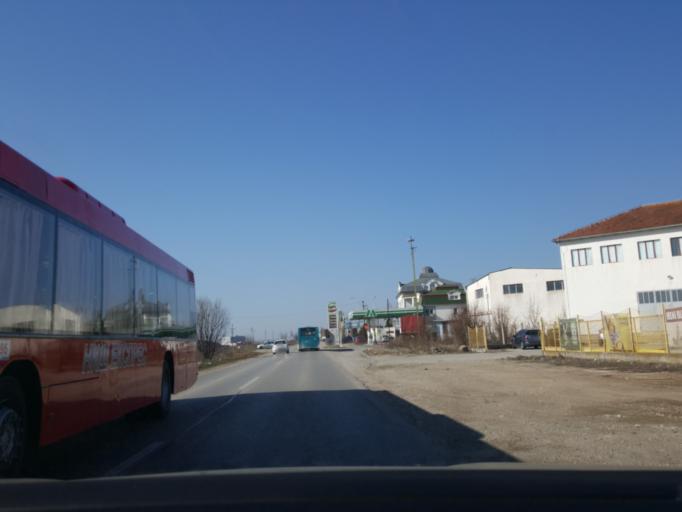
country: RS
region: Central Serbia
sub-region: Nisavski Okrug
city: Nis
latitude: 43.3557
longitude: 21.8531
